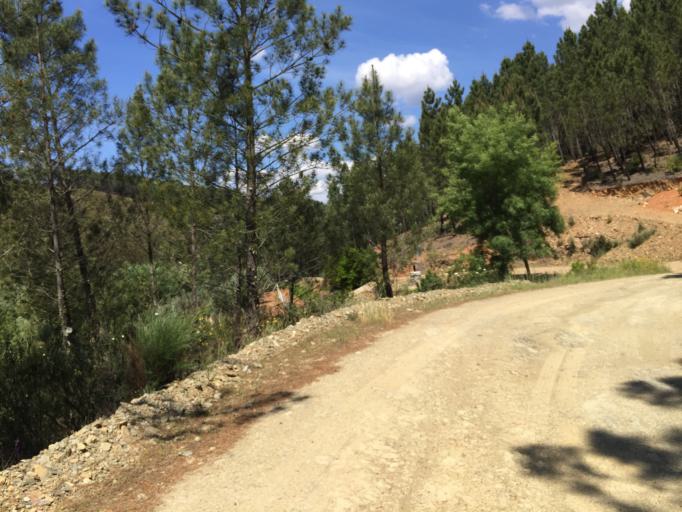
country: PT
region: Coimbra
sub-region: Pampilhosa da Serra
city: Pampilhosa da Serra
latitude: 40.0704
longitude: -7.7810
